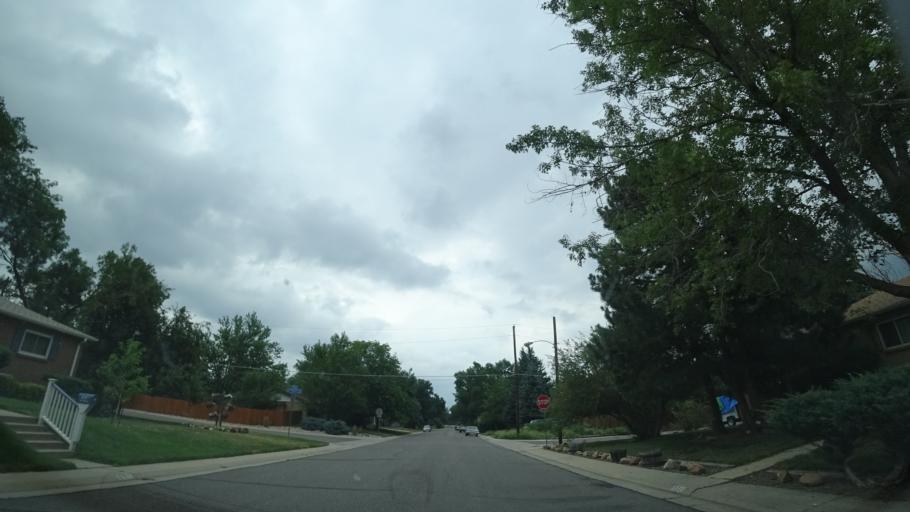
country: US
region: Colorado
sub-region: Jefferson County
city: Lakewood
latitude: 39.7070
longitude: -105.1304
